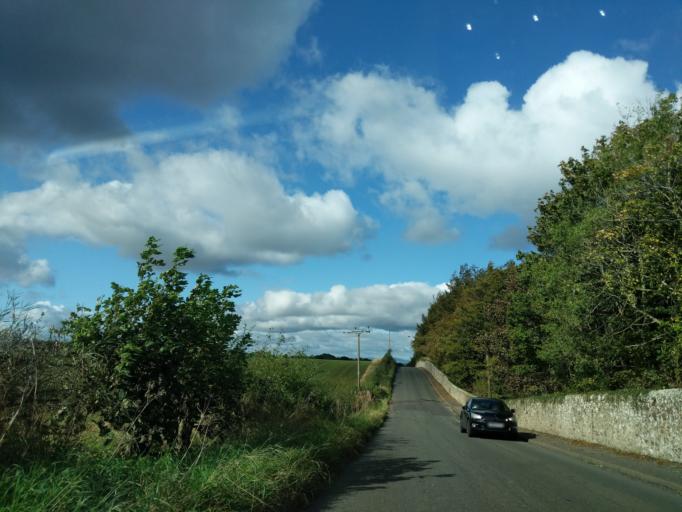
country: GB
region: Scotland
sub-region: Edinburgh
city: Currie
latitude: 55.9060
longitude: -3.3279
